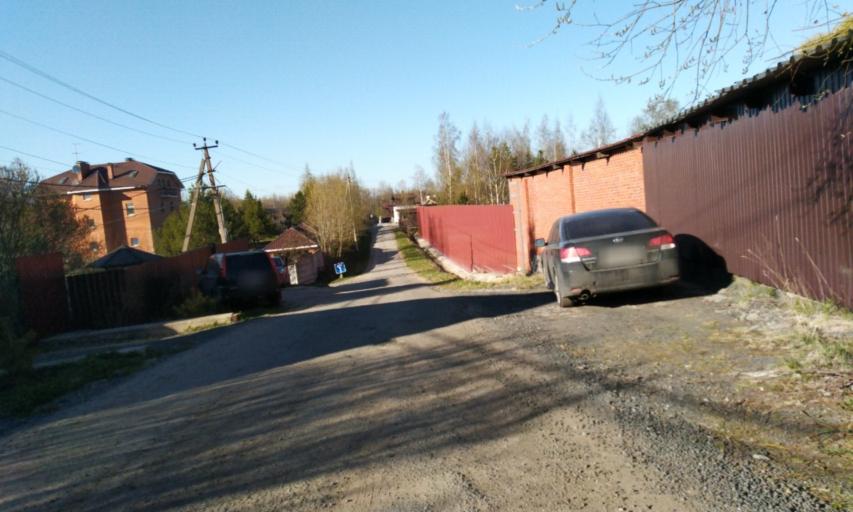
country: RU
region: Leningrad
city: Toksovo
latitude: 60.1505
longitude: 30.5695
